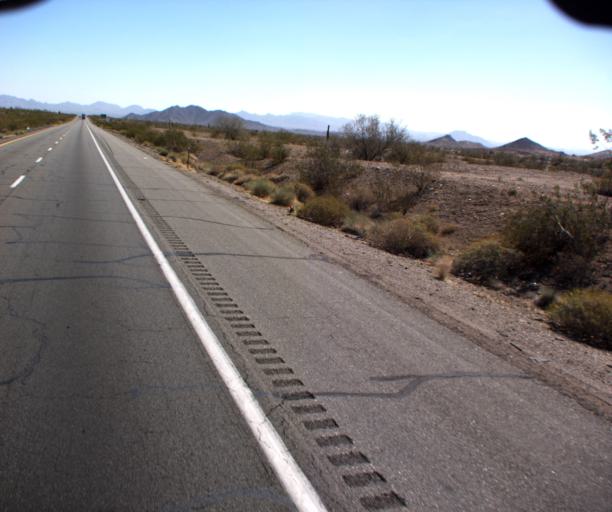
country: US
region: Arizona
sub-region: La Paz County
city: Quartzsite
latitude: 33.6472
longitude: -114.3274
